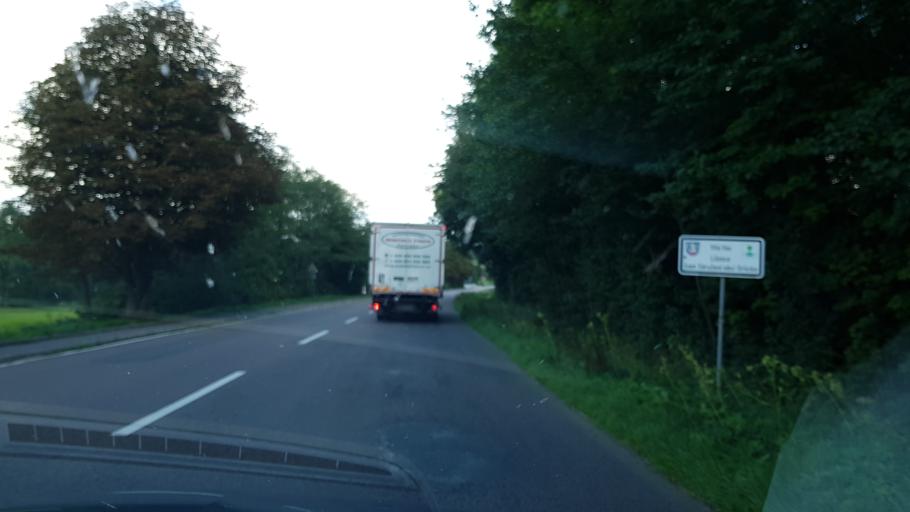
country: CZ
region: Pardubicky
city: Zamberk
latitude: 50.0838
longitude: 16.4924
